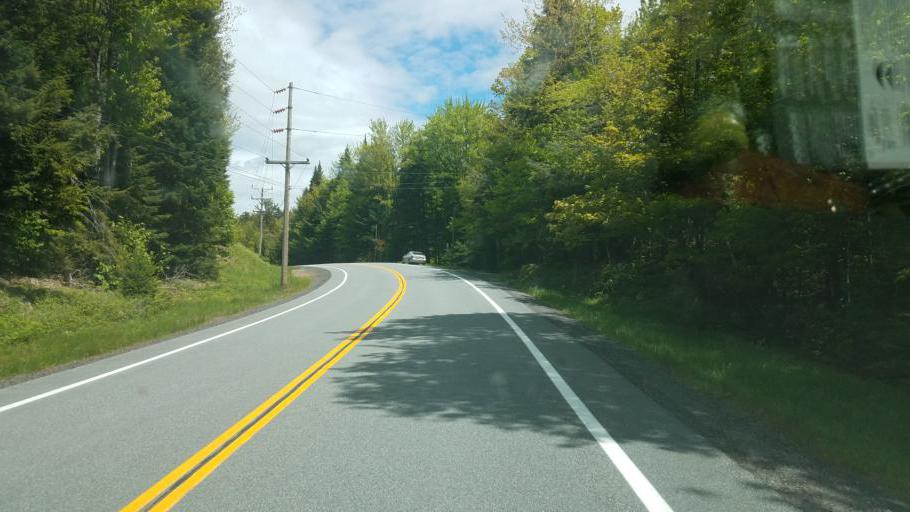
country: US
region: New York
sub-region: Hamilton County
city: Lake Pleasant
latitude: 43.8125
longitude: -74.5969
